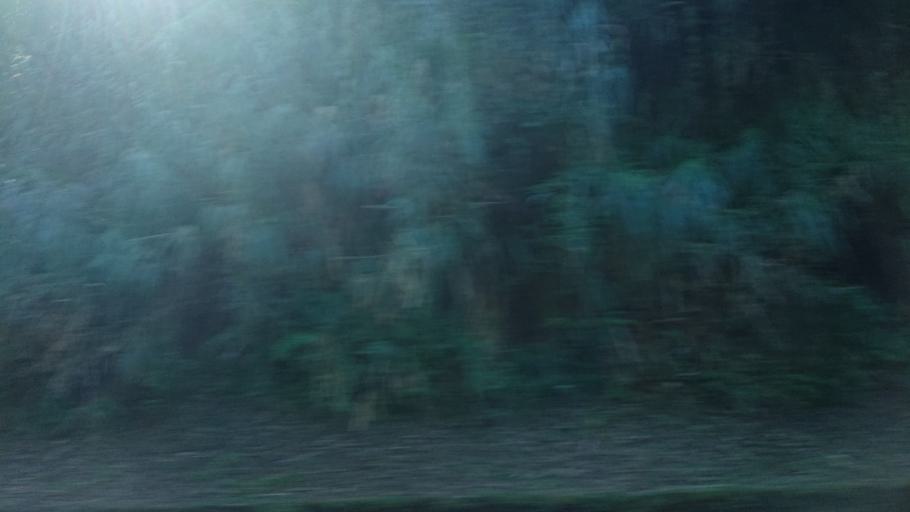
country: TW
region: Taiwan
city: Lugu
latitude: 23.4811
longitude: 120.8330
